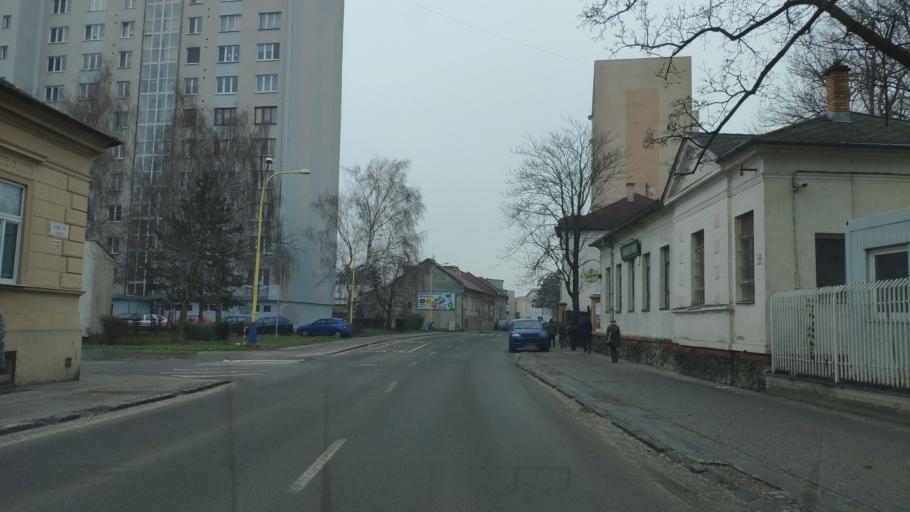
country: SK
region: Kosicky
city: Kosice
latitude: 48.7312
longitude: 21.2609
